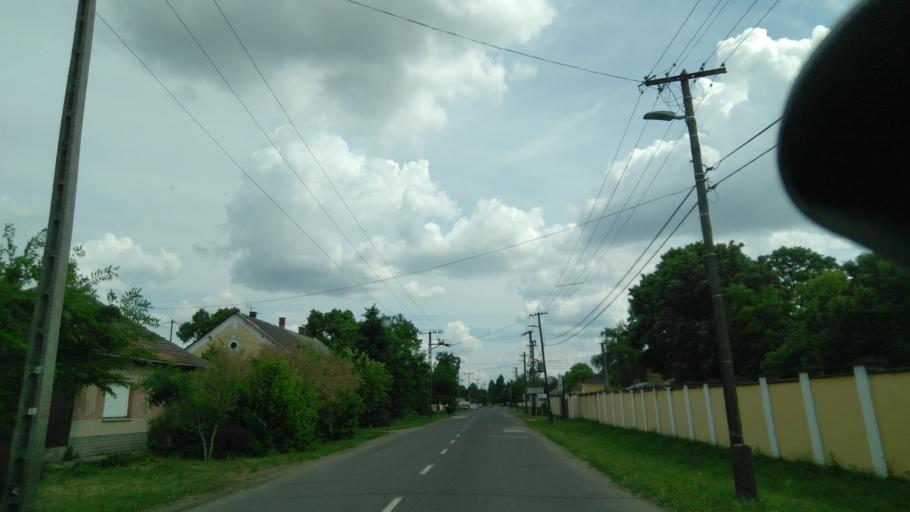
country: HU
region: Bekes
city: Mezohegyes
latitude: 46.3210
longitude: 20.8189
